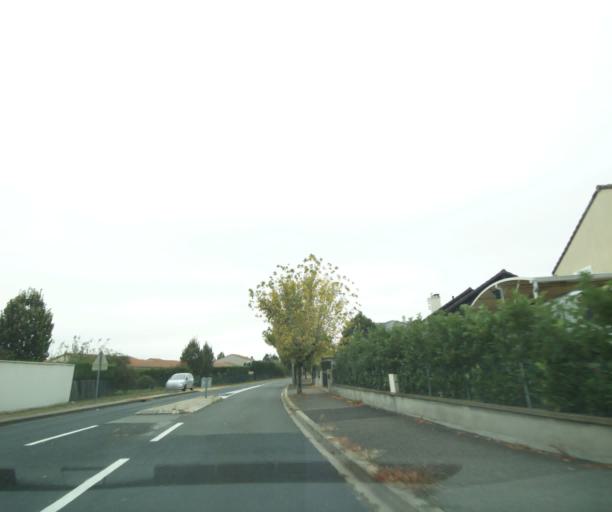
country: FR
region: Auvergne
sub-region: Departement du Puy-de-Dome
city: Gerzat
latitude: 45.8369
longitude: 3.1497
